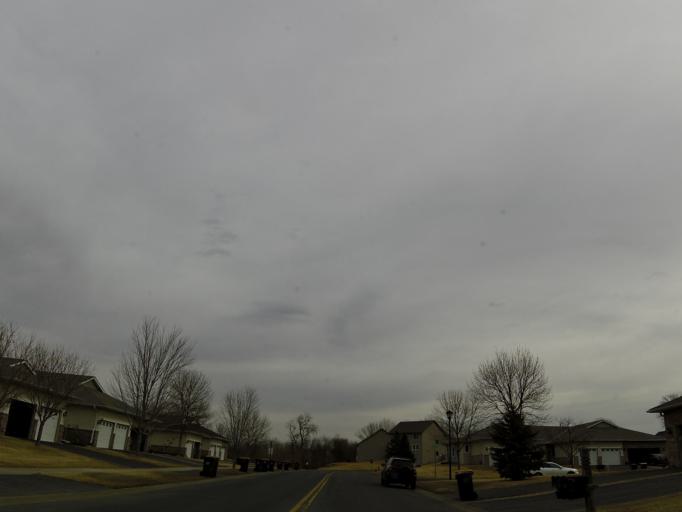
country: US
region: Minnesota
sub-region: Scott County
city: Savage
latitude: 44.7663
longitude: -93.3906
